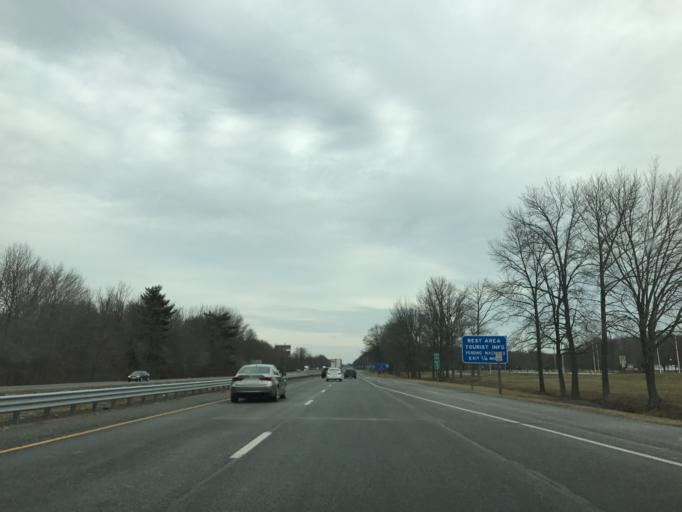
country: US
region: New Jersey
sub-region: Salem County
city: Carneys Point
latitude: 39.6860
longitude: -75.4775
